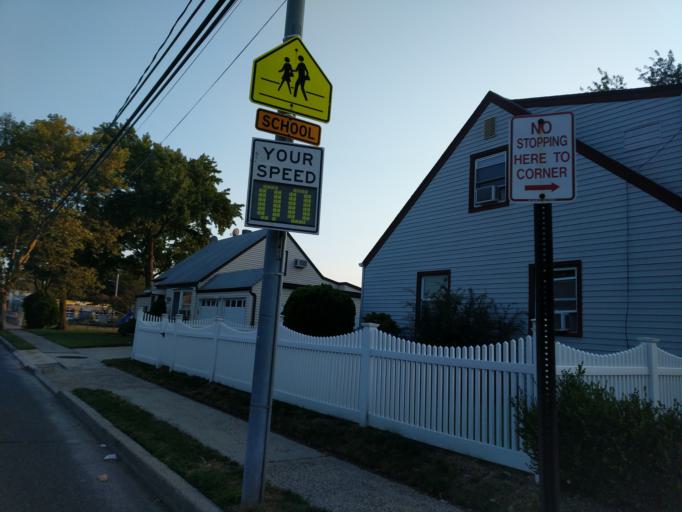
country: US
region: New York
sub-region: Nassau County
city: South Valley Stream
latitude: 40.6555
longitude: -73.7095
